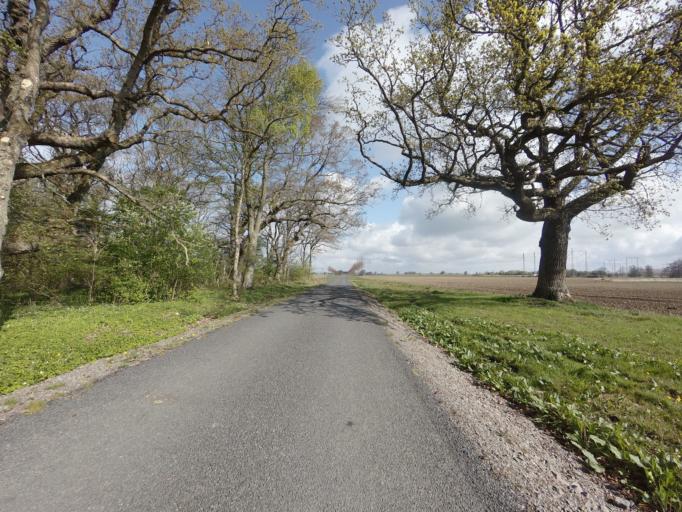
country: SE
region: Skane
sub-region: Hoganas Kommun
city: Hoganas
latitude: 56.1341
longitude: 12.6139
